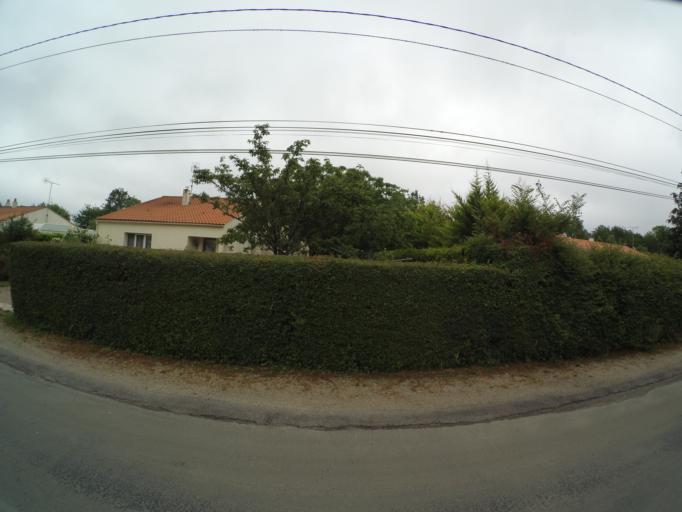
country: FR
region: Pays de la Loire
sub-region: Departement de la Vendee
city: La Roche-sur-Yon
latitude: 46.6364
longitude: -1.4309
